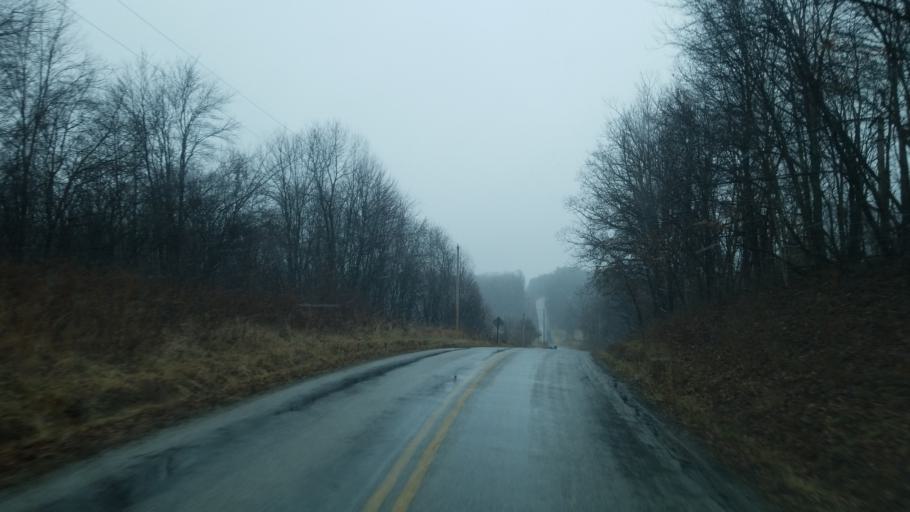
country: US
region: Ohio
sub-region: Licking County
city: Utica
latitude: 40.2207
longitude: -82.3371
